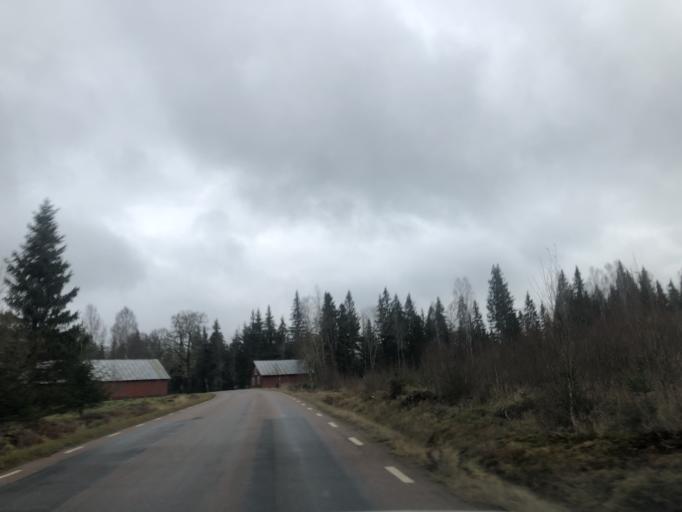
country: SE
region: Vaestra Goetaland
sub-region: Ulricehamns Kommun
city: Ulricehamn
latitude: 57.8302
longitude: 13.5000
